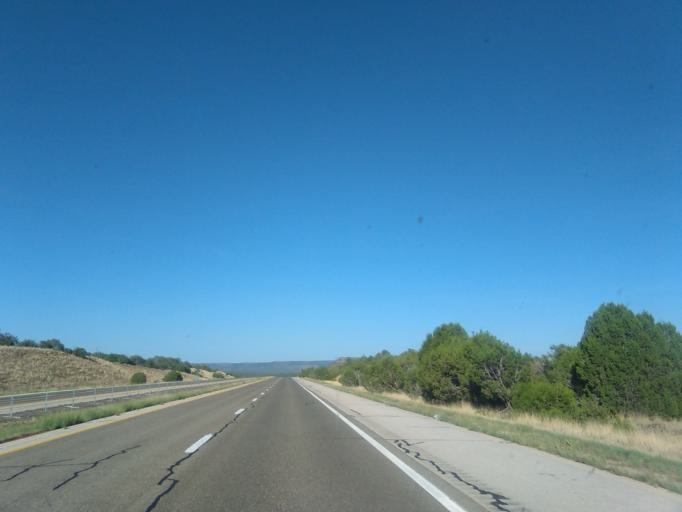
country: US
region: New Mexico
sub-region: San Miguel County
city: Las Vegas
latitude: 35.3925
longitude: -105.3398
